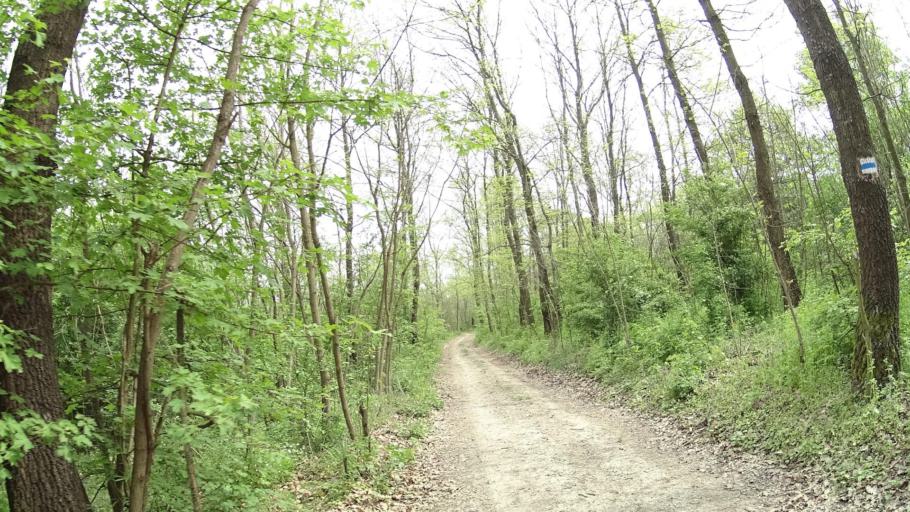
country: HU
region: Nograd
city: Romhany
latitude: 47.9279
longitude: 19.3017
